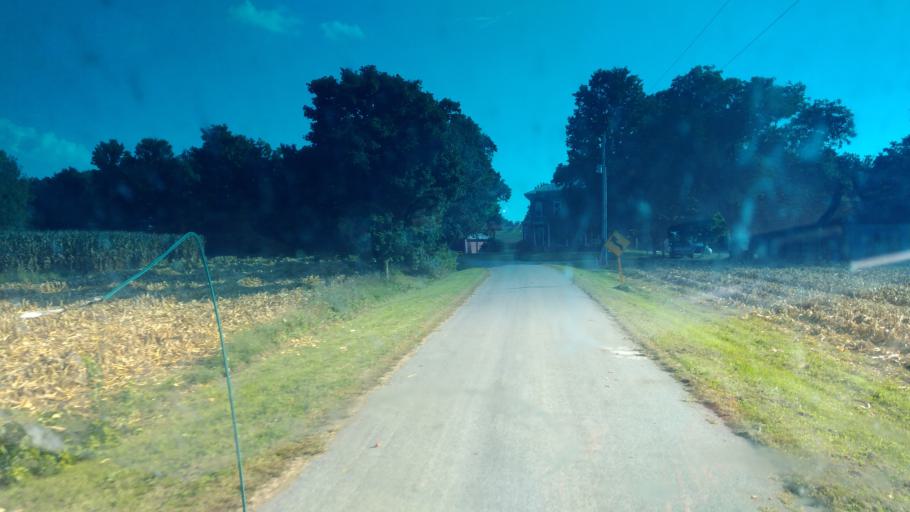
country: US
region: Ohio
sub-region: Wyandot County
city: Upper Sandusky
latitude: 40.9048
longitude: -83.2447
